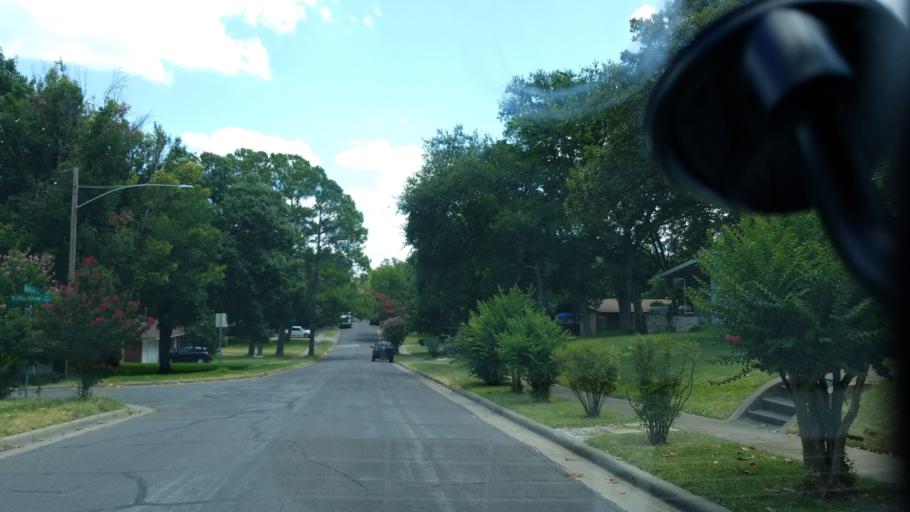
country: US
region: Texas
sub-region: Dallas County
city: Cockrell Hill
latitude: 32.7064
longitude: -96.8461
